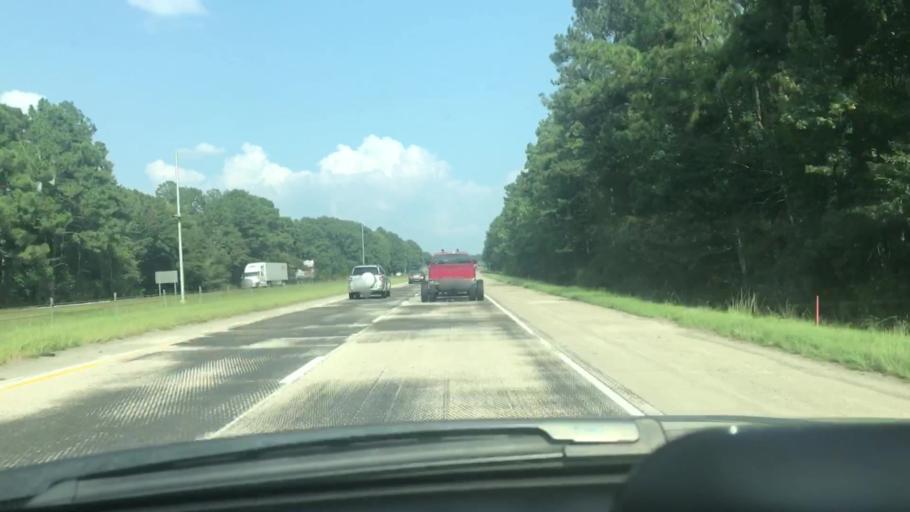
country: US
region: Louisiana
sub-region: Tangipahoa Parish
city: Hammond
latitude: 30.4794
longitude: -90.5098
